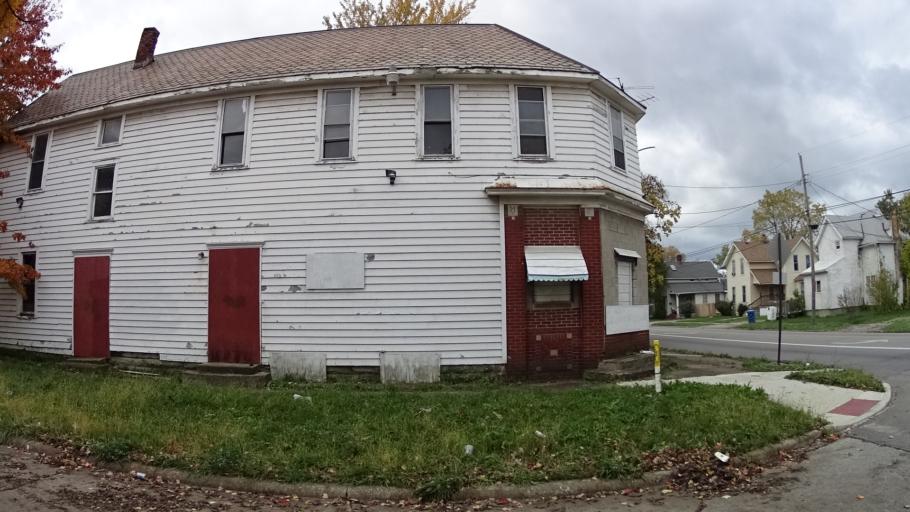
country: US
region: Ohio
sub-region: Lorain County
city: Lorain
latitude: 41.4510
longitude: -82.1701
